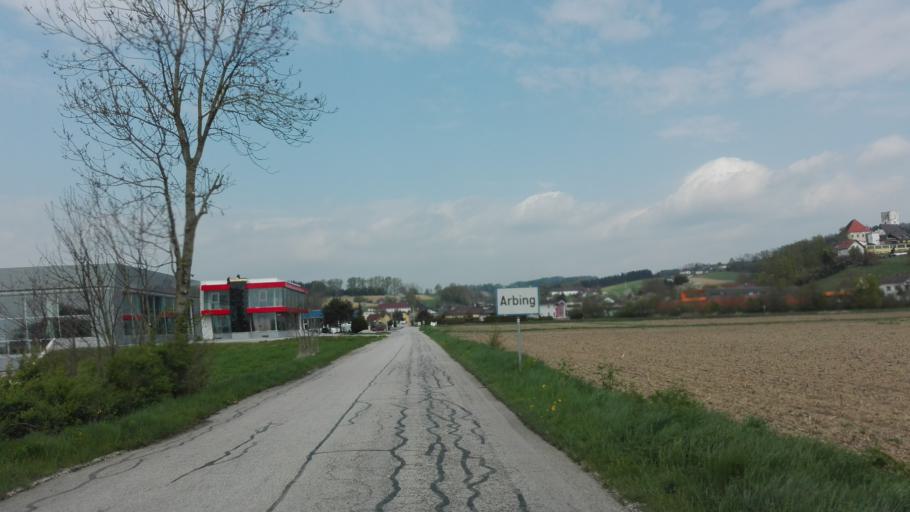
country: AT
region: Upper Austria
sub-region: Politischer Bezirk Perg
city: Perg
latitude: 48.2234
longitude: 14.7009
